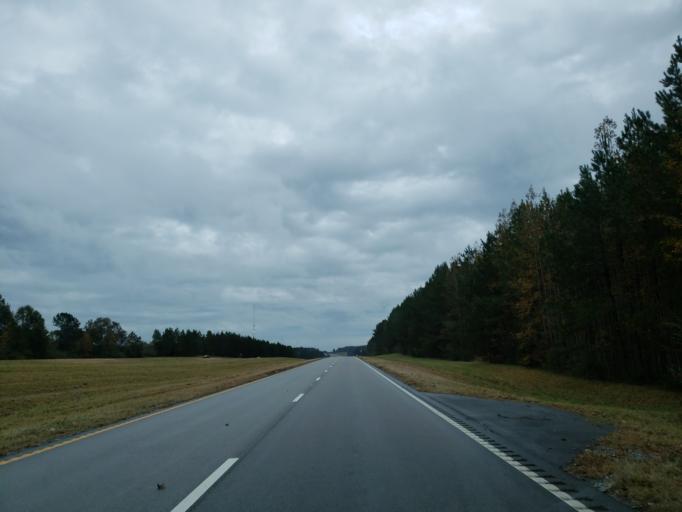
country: US
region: Mississippi
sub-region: Wayne County
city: Waynesboro
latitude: 31.6930
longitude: -88.7163
